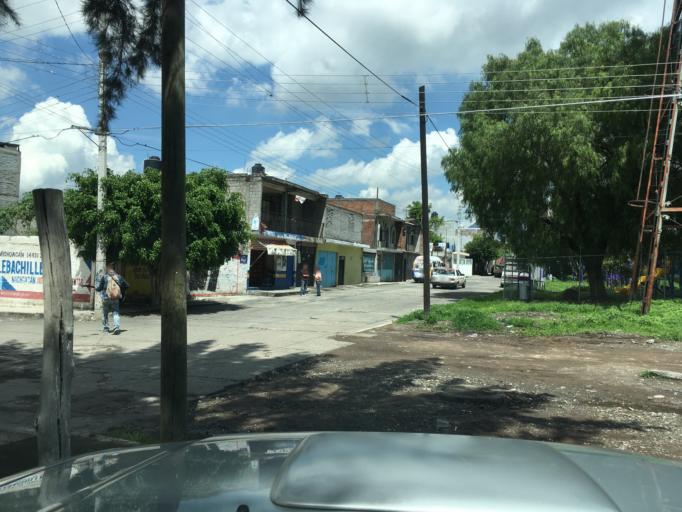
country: MX
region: Michoacan
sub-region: Tarimbaro
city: Real Hacienda (Metropolis)
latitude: 19.7289
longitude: -101.2033
